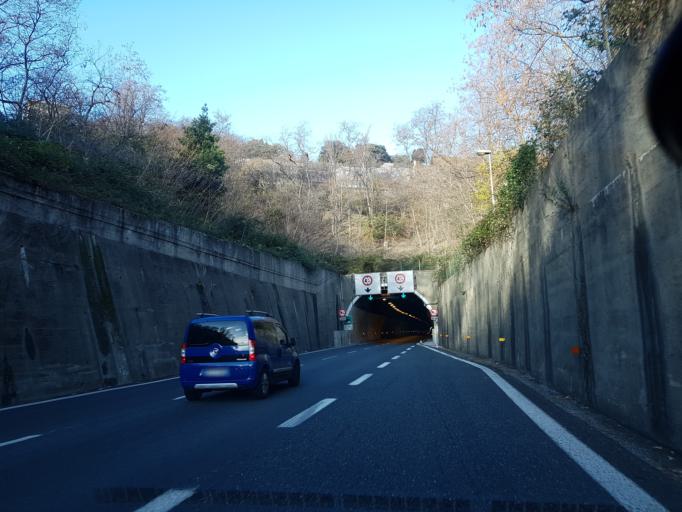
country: IT
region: Liguria
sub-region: Provincia di Genova
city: Genoa
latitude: 44.4460
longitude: 8.9039
